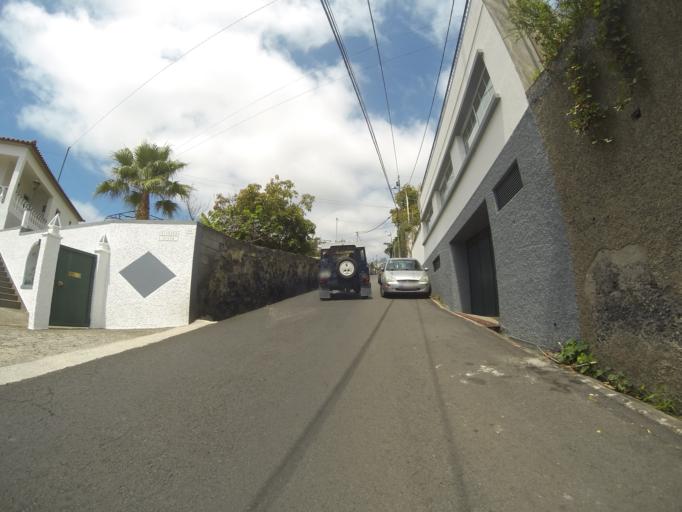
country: PT
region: Madeira
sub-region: Funchal
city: Nossa Senhora do Monte
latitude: 32.6681
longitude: -16.9327
